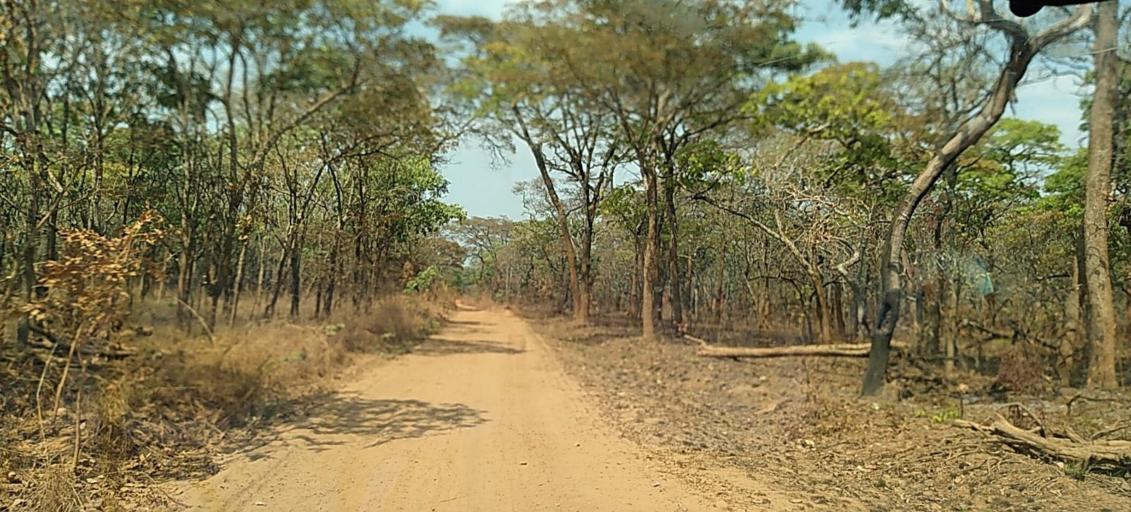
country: ZM
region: North-Western
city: Kasempa
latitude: -13.3197
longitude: 26.0485
